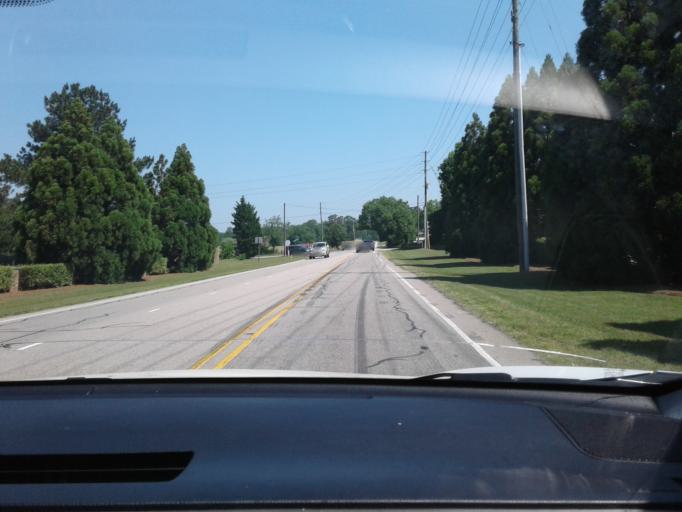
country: US
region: North Carolina
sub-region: Wake County
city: Fuquay-Varina
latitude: 35.6032
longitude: -78.8395
